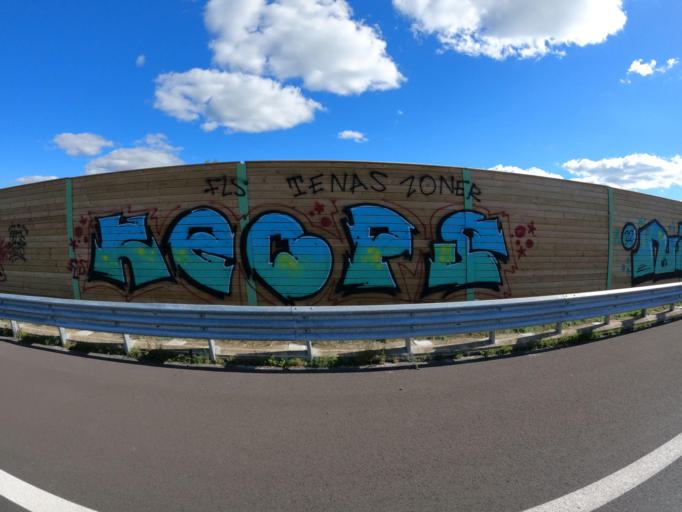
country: FR
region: Auvergne
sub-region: Departement de l'Allier
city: Souvigny
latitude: 46.4544
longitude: 3.2354
